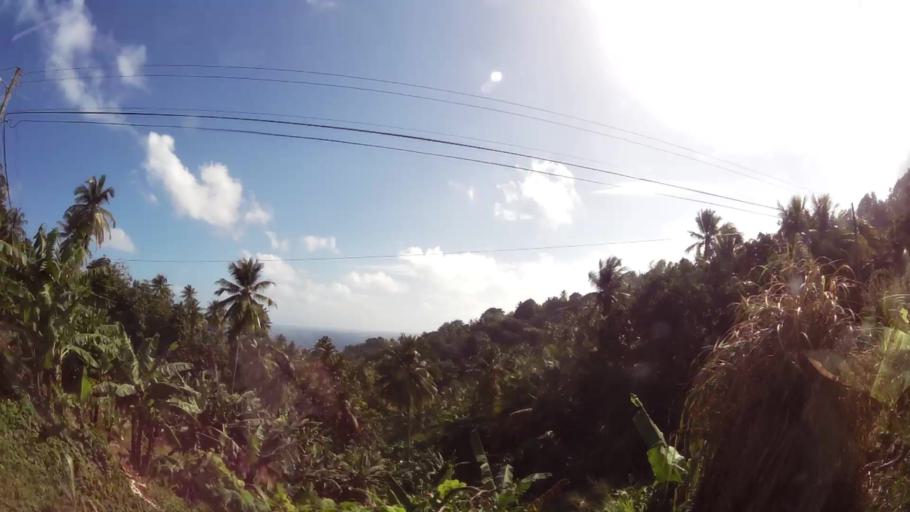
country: DM
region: Saint David
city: Castle Bruce
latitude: 15.4857
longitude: -61.2557
